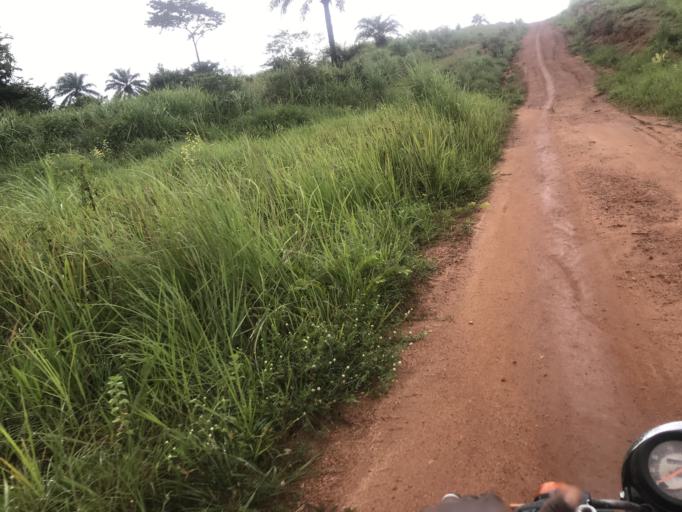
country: GN
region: Nzerekore
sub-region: Prefecture de Guekedou
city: Gueckedou
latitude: 8.4770
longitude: -10.2923
